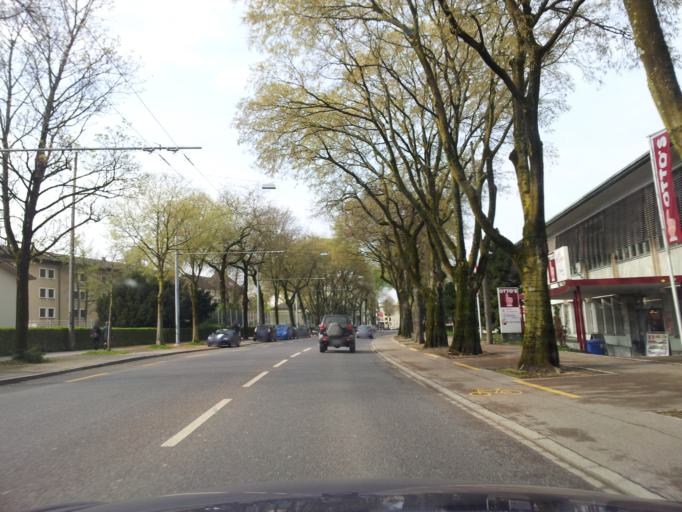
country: CH
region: Bern
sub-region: Biel/Bienne District
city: Biel/Bienne
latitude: 47.1448
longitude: 7.2524
